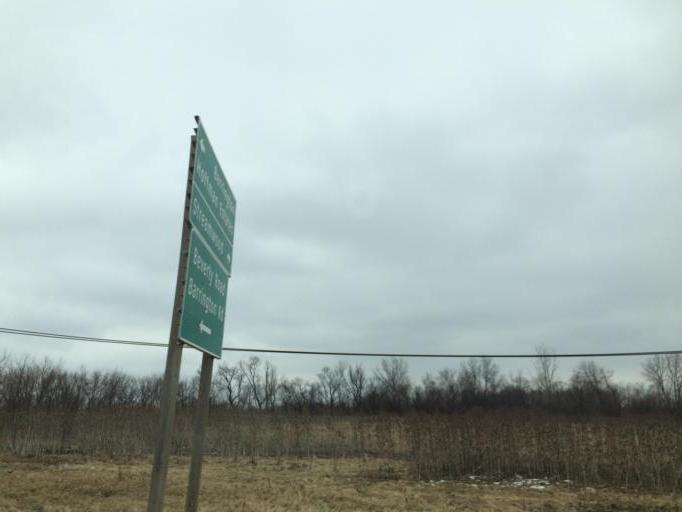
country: US
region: Illinois
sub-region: Cook County
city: Streamwood
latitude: 42.0646
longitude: -88.1956
